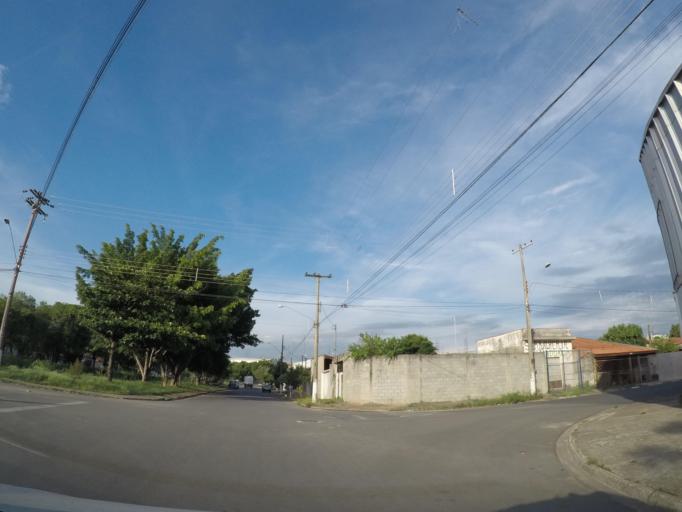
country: BR
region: Sao Paulo
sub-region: Sumare
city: Sumare
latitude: -22.8139
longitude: -47.2636
